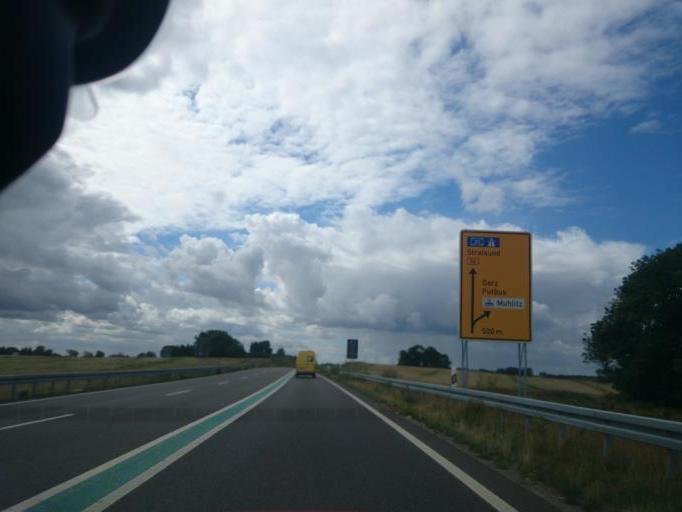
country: DE
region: Mecklenburg-Vorpommern
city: Samtens
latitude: 54.3544
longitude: 13.3040
